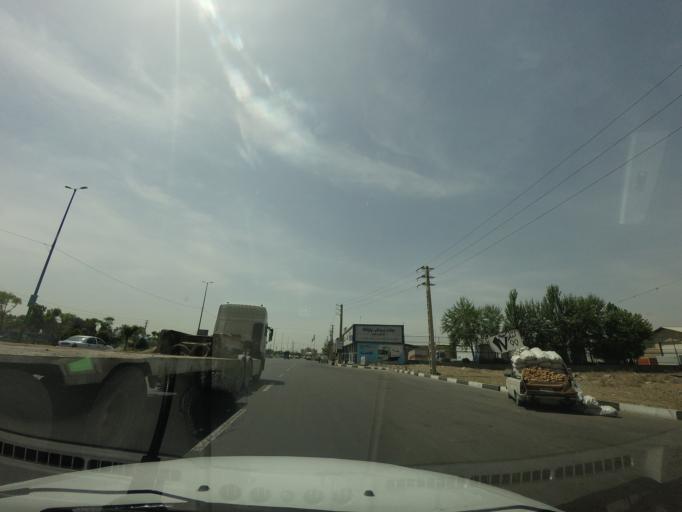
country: IR
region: Tehran
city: Eslamshahr
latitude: 35.5673
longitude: 51.2596
